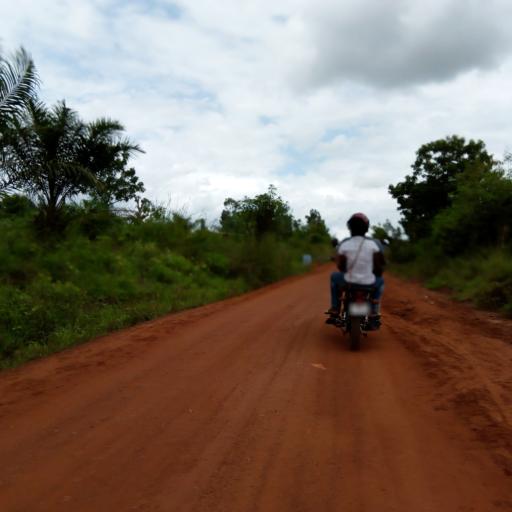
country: TG
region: Maritime
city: Tsevie
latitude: 6.3378
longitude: 1.0945
